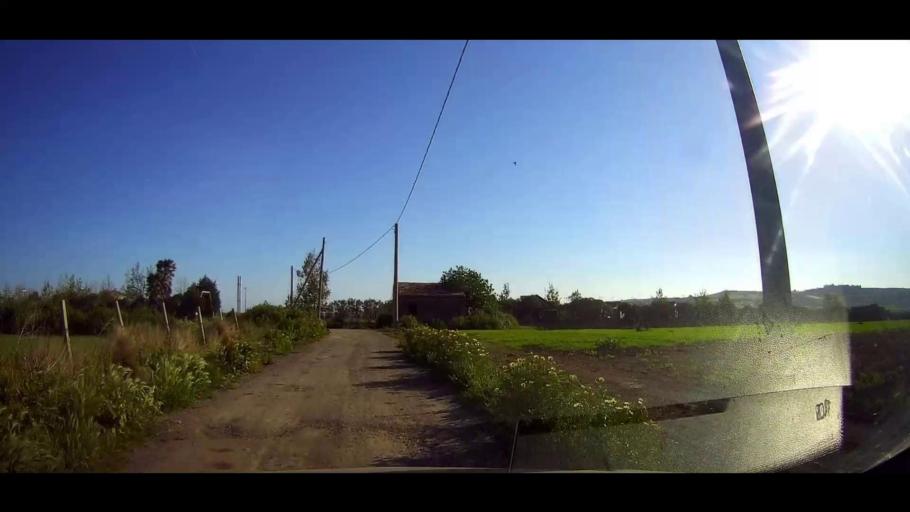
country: IT
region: Calabria
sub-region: Provincia di Crotone
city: Crotone
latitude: 39.0212
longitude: 17.1864
